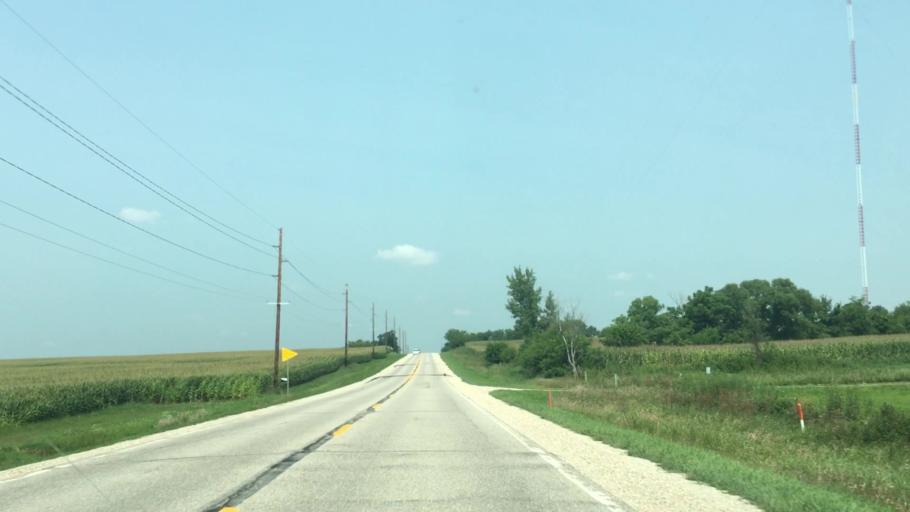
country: US
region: Iowa
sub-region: Benton County
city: Urbana
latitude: 42.2902
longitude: -91.8899
